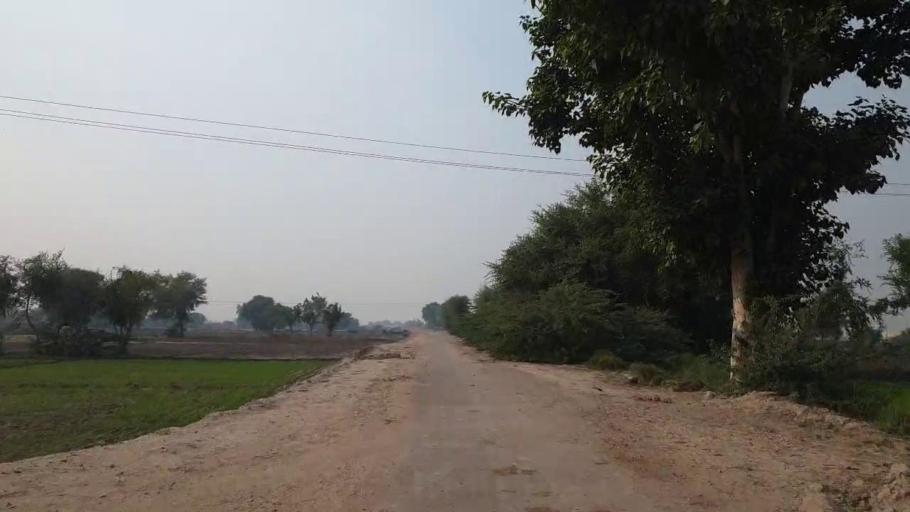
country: PK
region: Sindh
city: Bhan
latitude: 26.5415
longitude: 67.7156
